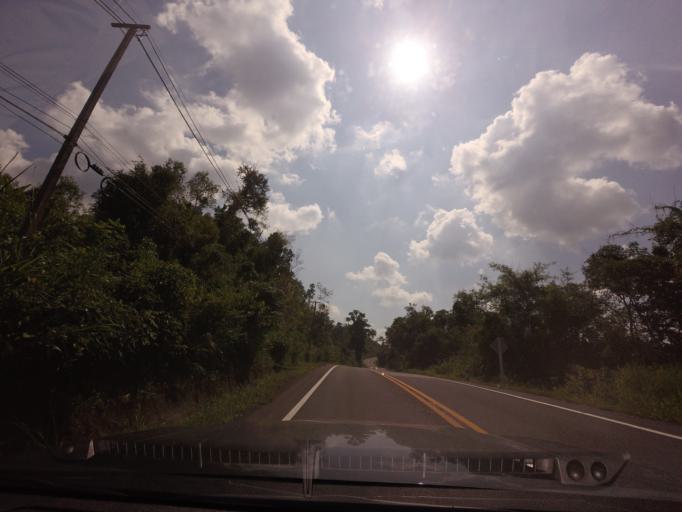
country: TH
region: Nan
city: Bo Kluea
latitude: 19.0805
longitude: 101.1443
